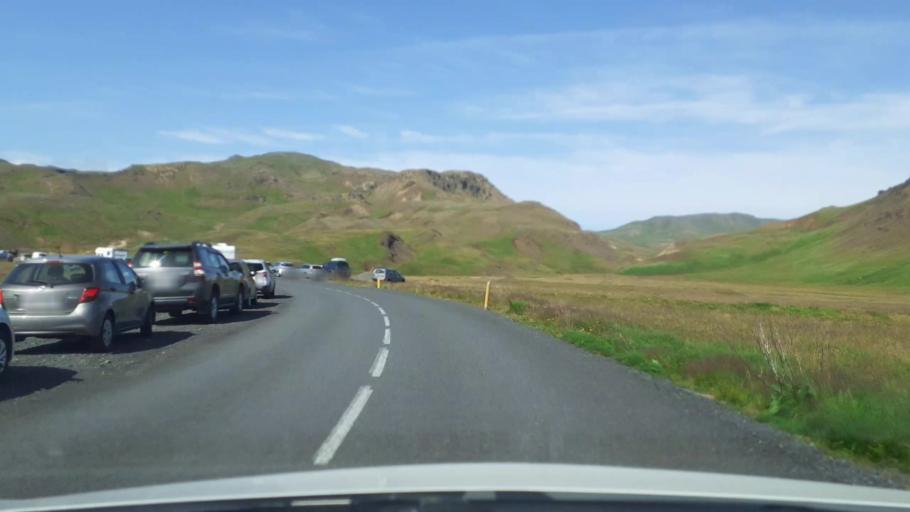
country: IS
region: South
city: Hveragerdi
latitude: 64.0188
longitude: -21.2069
